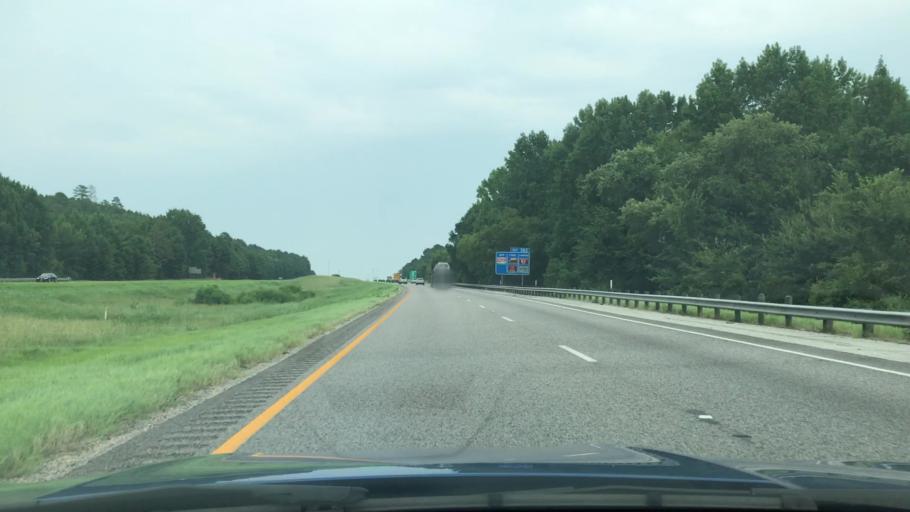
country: US
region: Texas
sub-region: Smith County
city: Tyler
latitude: 32.4562
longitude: -95.3036
